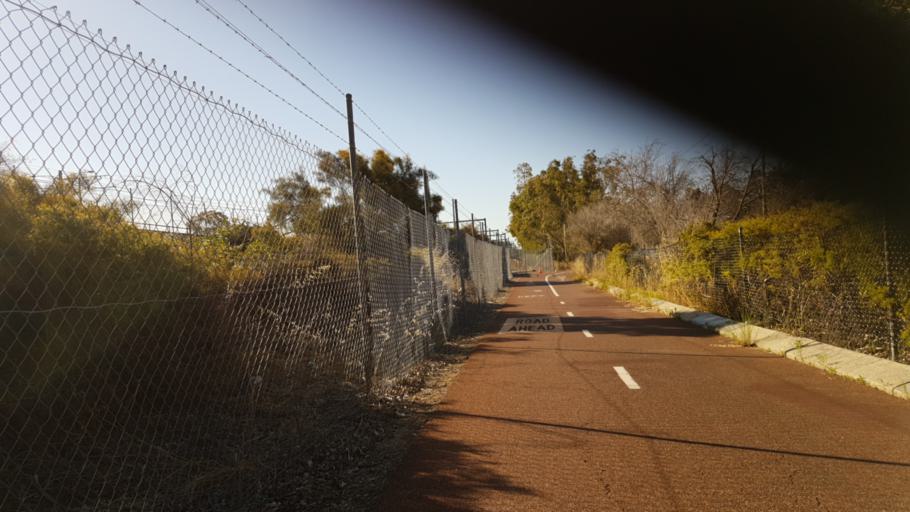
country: AU
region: Western Australia
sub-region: Gosnells
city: Kenwick
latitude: -32.0306
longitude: 115.9635
